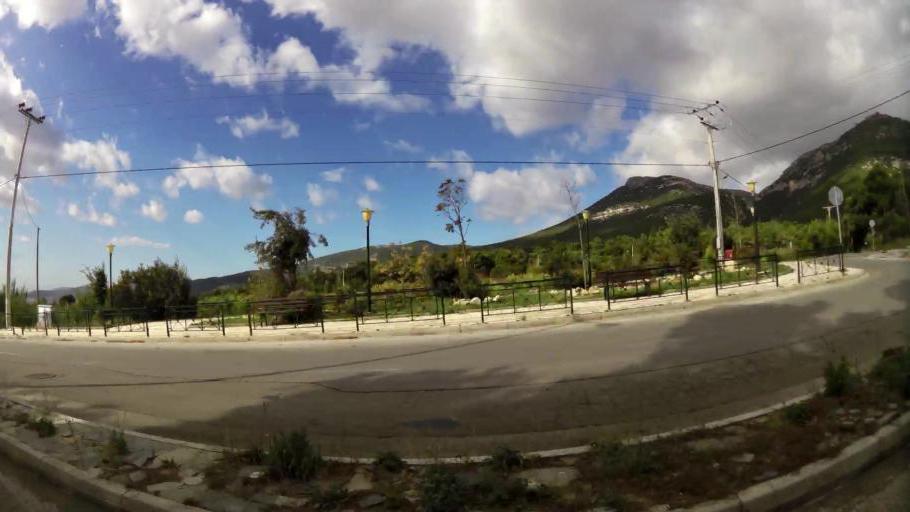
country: GR
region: Attica
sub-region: Nomarchia Anatolikis Attikis
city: Thrakomakedones
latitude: 38.1366
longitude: 23.7509
